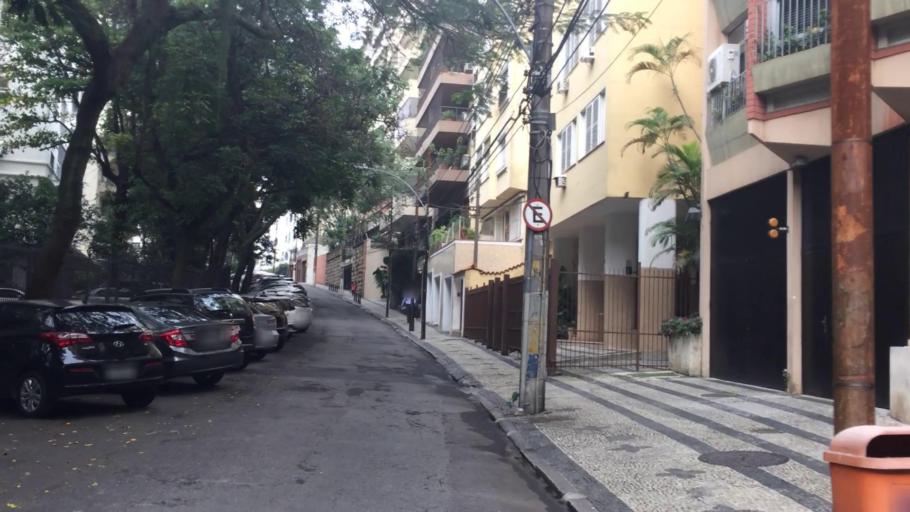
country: BR
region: Rio de Janeiro
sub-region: Rio De Janeiro
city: Rio de Janeiro
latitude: -22.9412
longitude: -43.1922
